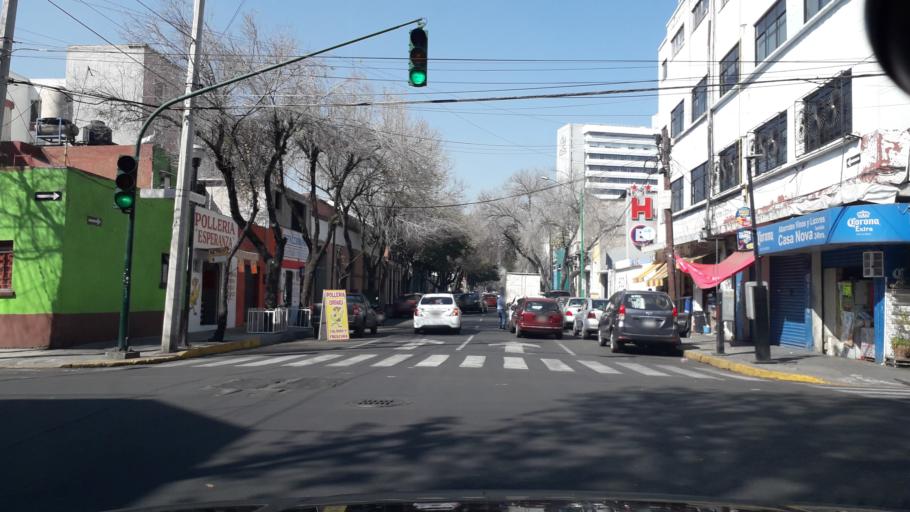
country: MX
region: Mexico City
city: Cuauhtemoc
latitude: 19.4436
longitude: -99.1493
